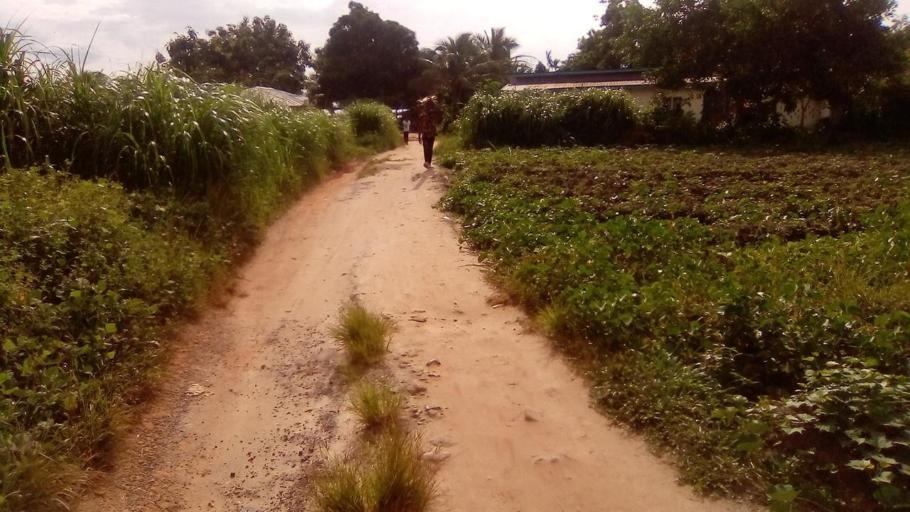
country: SL
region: Southern Province
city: Pujehun
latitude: 7.3637
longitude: -11.7237
